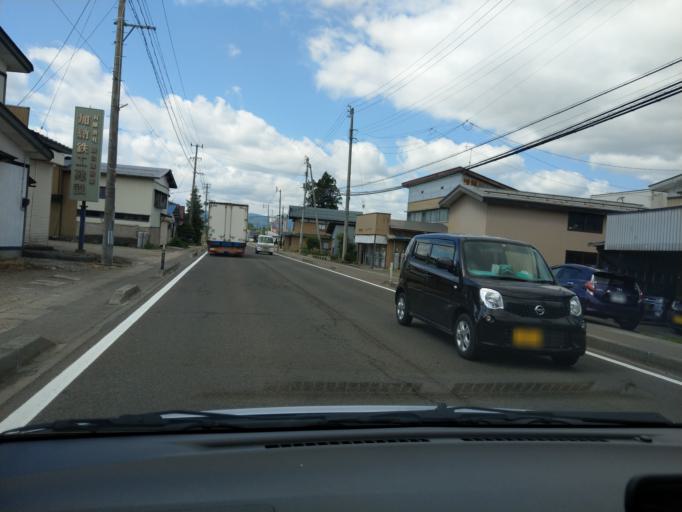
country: JP
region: Akita
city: Yuzawa
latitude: 39.1867
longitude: 140.5001
